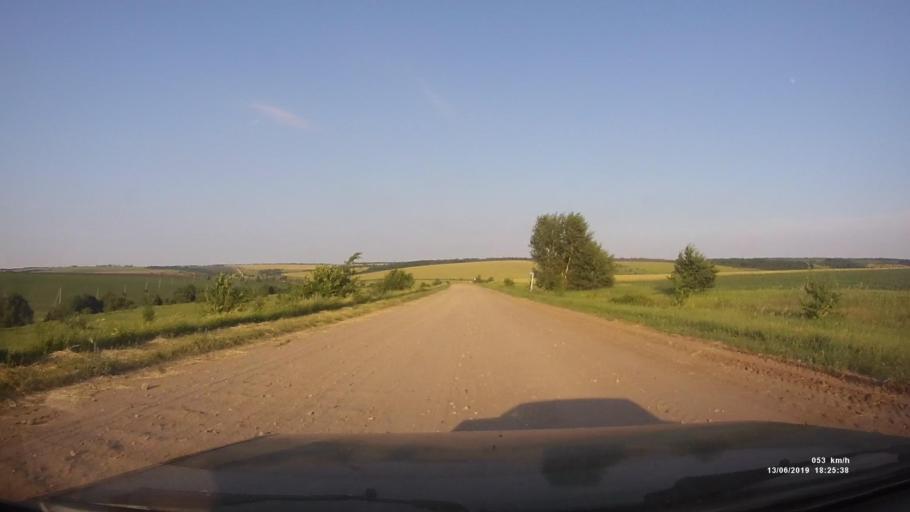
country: RU
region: Rostov
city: Kazanskaya
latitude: 49.8508
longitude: 41.3035
